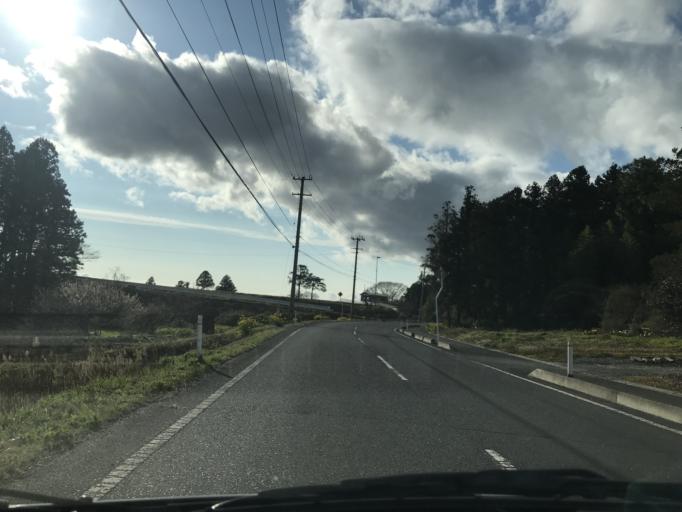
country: JP
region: Miyagi
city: Wakuya
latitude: 38.6215
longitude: 141.2272
